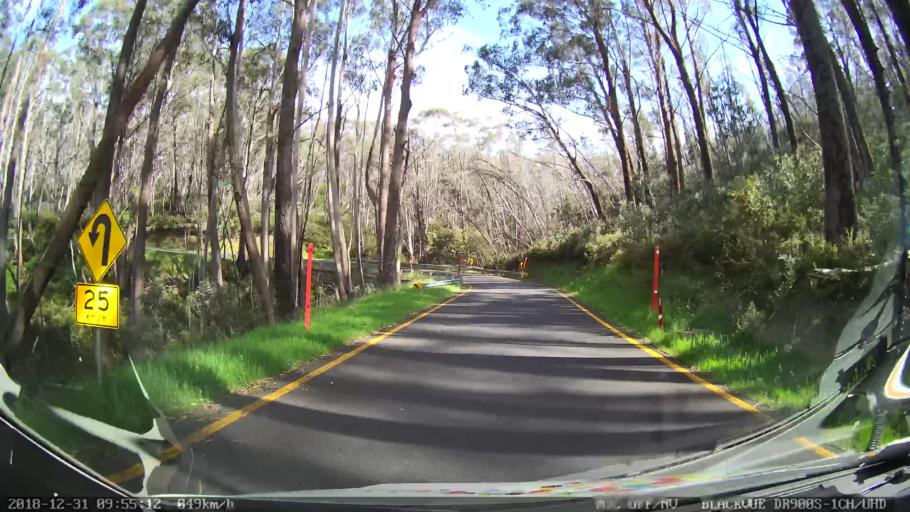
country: AU
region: New South Wales
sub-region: Snowy River
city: Jindabyne
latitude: -36.5320
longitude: 148.2309
